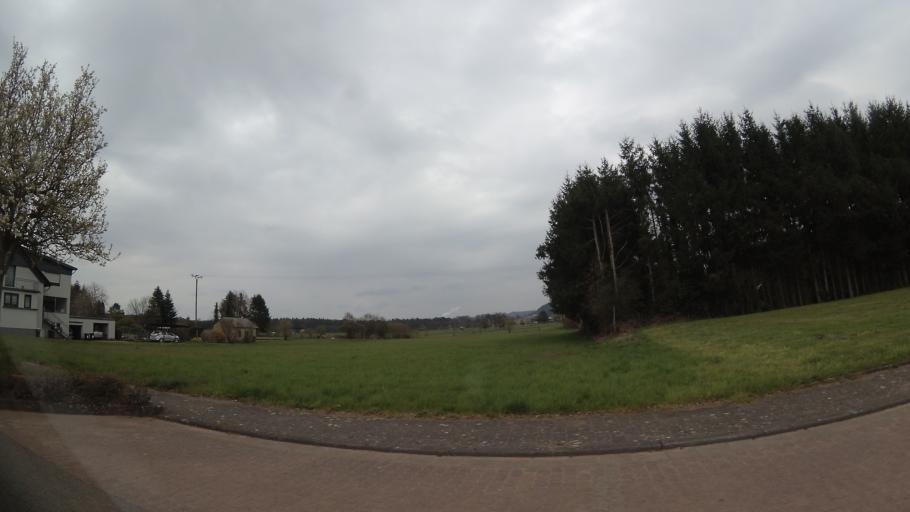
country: DE
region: Saarland
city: Losheim
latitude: 49.5065
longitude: 6.7824
